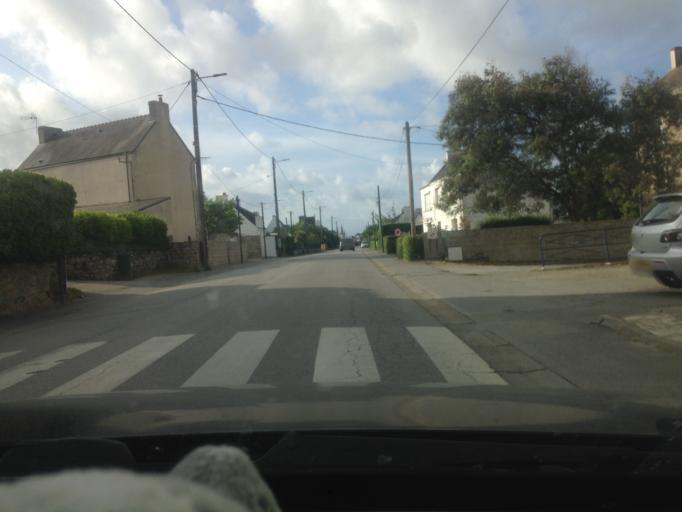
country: FR
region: Brittany
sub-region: Departement du Morbihan
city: Plouharnel
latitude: 47.6035
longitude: -3.1185
